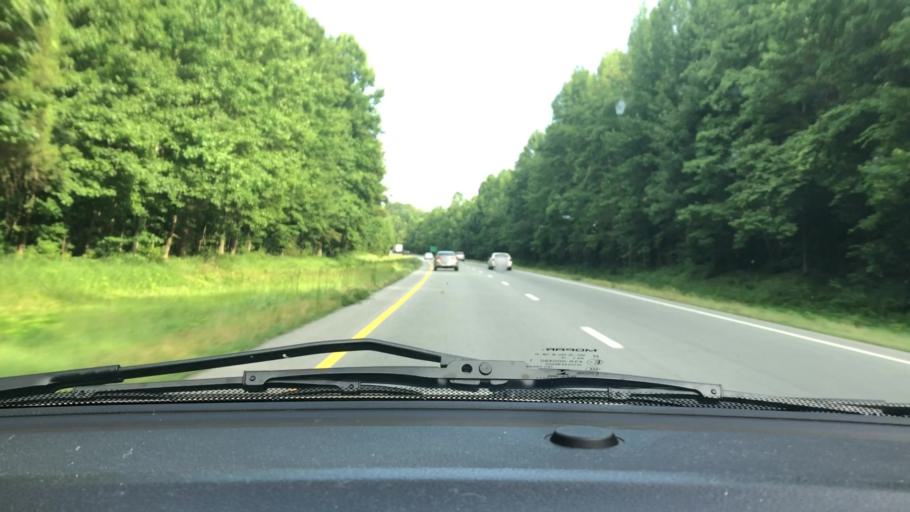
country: US
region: North Carolina
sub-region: Randolph County
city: Liberty
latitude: 35.8657
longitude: -79.6266
